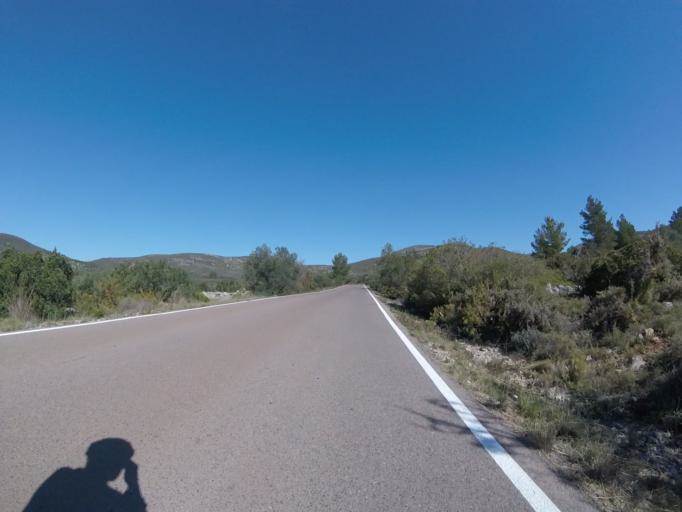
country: ES
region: Valencia
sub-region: Provincia de Castello
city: Santa Magdalena de Pulpis
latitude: 40.3750
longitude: 0.2717
